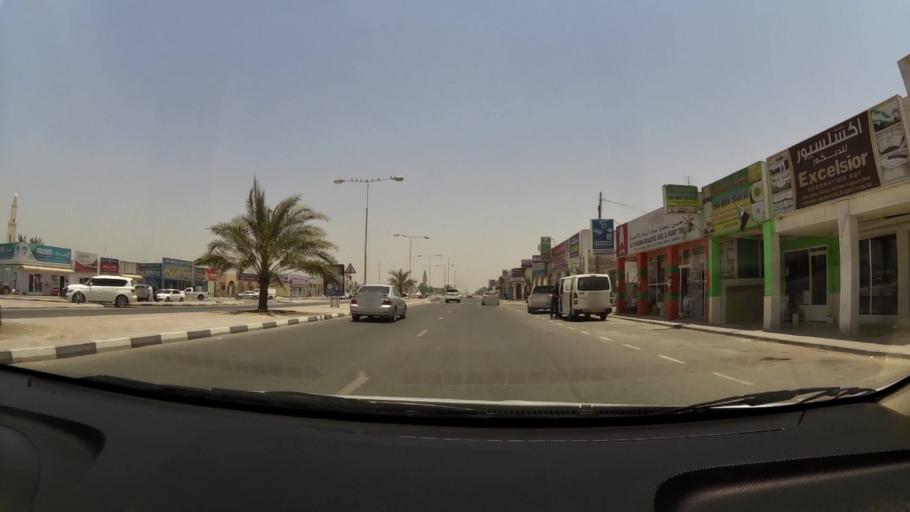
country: AE
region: Umm al Qaywayn
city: Umm al Qaywayn
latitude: 25.5516
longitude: 55.5510
